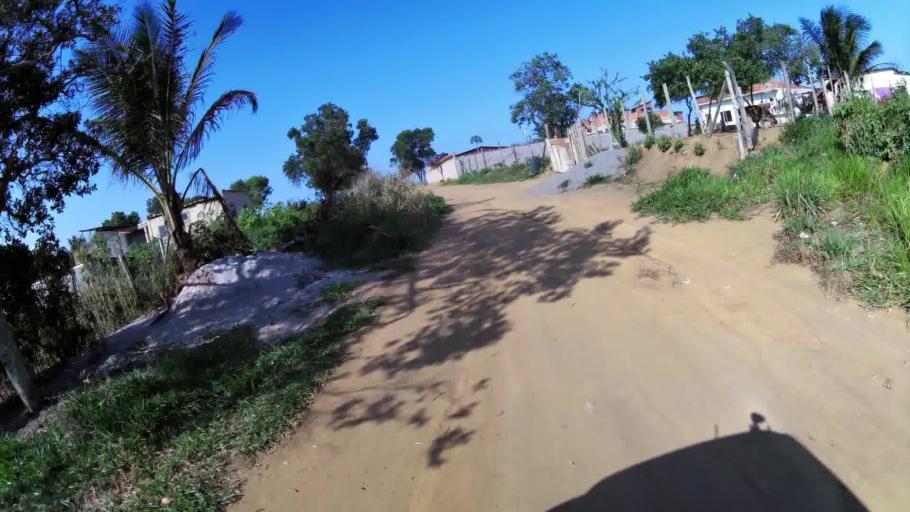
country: BR
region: Espirito Santo
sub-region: Guarapari
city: Guarapari
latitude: -20.7189
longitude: -40.5320
